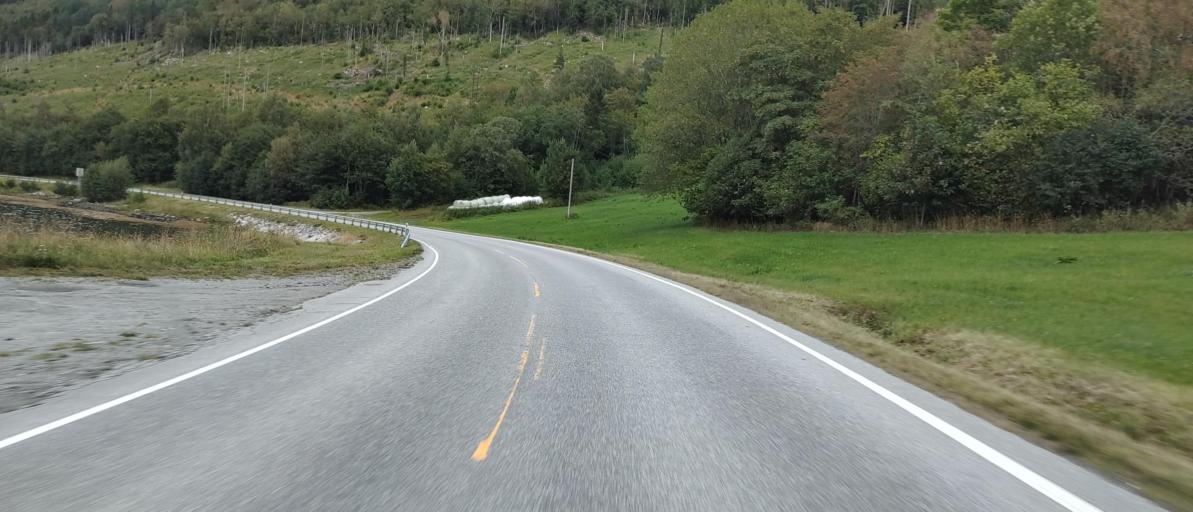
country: NO
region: More og Romsdal
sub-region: Rauma
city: Andalsnes
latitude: 62.5893
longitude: 7.5438
